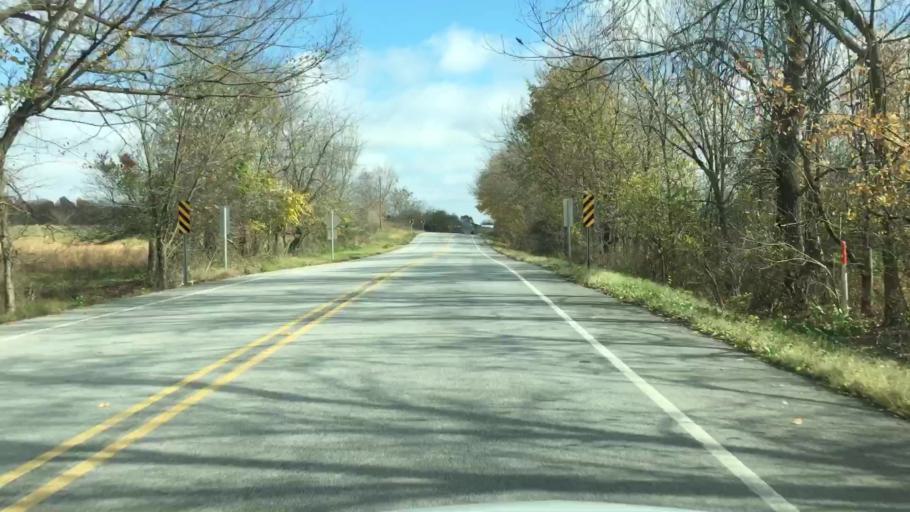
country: US
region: Arkansas
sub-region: Benton County
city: Centerton
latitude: 36.3023
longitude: -94.3190
